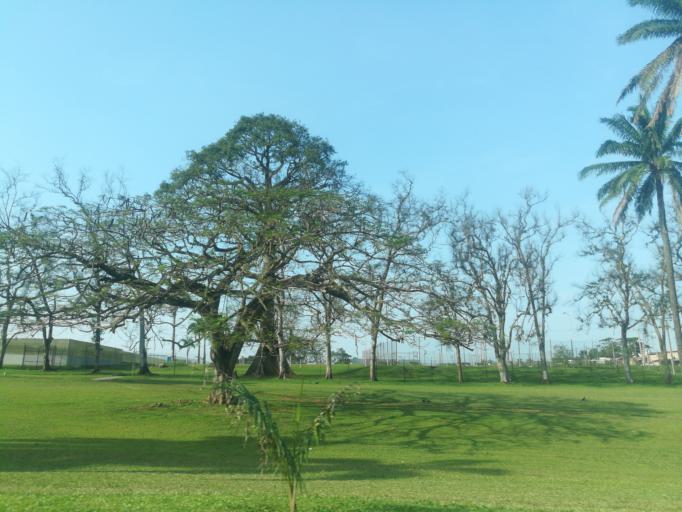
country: NG
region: Oyo
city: Moniya
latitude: 7.4999
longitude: 3.9126
